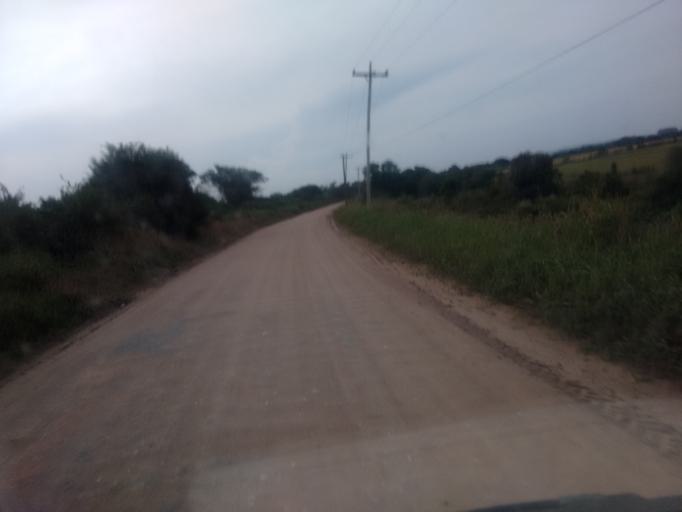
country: BR
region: Rio Grande do Sul
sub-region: Camaqua
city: Camaqua
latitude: -30.9139
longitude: -51.8068
